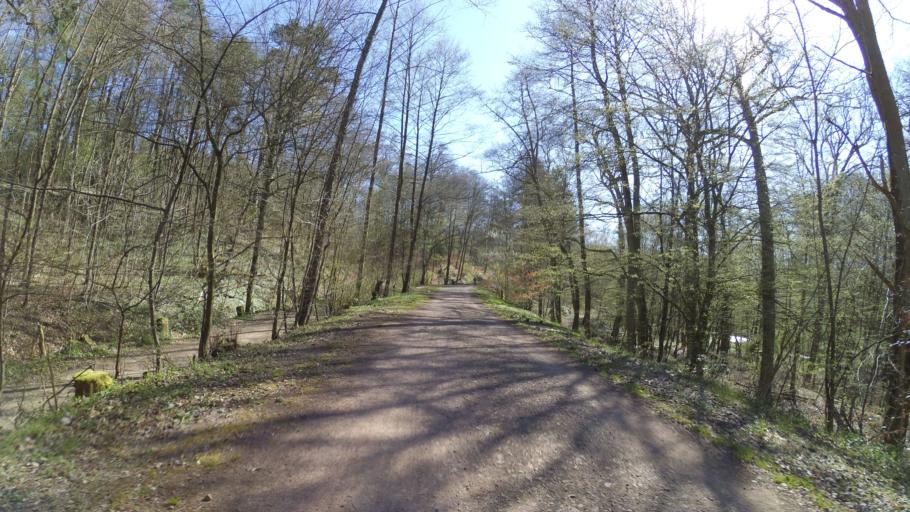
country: DE
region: Saarland
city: Volklingen
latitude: 49.2627
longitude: 6.8794
